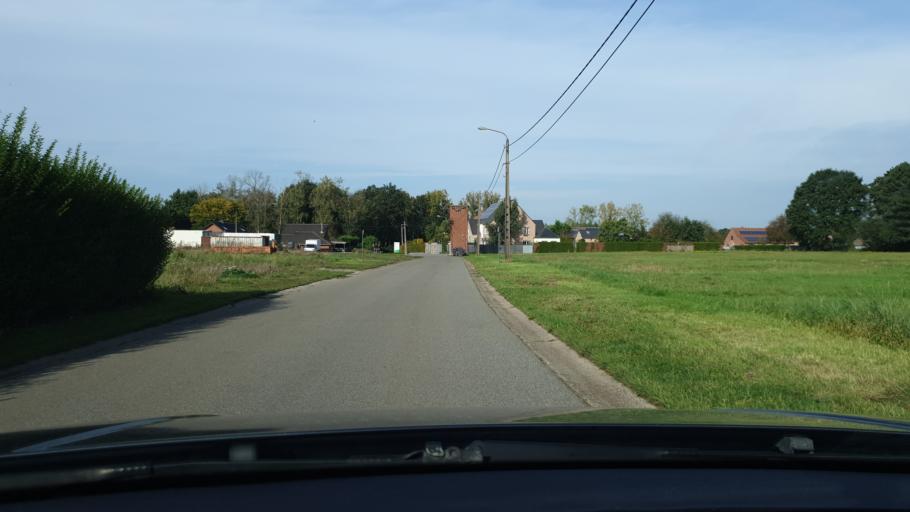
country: BE
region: Flanders
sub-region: Provincie Antwerpen
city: Meerhout
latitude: 51.1229
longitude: 5.0499
